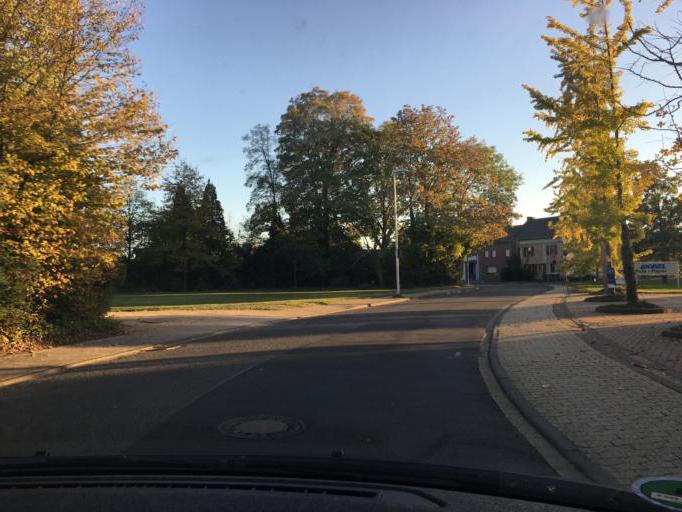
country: DE
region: North Rhine-Westphalia
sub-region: Regierungsbezirk Koln
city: Dueren
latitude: 50.8131
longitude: 6.4451
